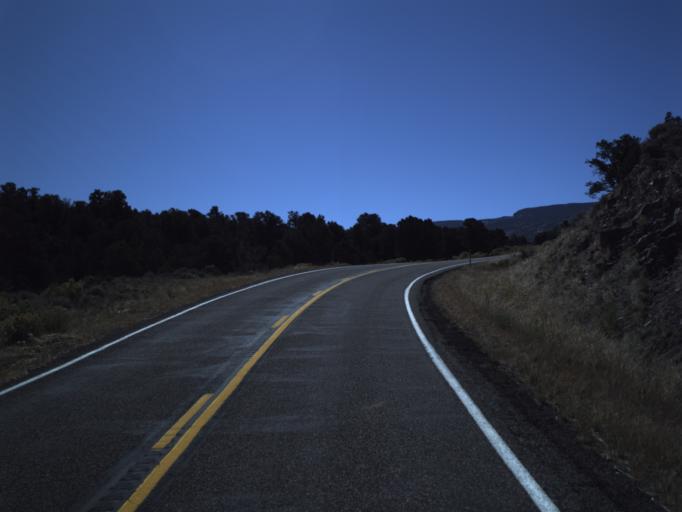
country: US
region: Utah
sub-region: Wayne County
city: Loa
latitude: 38.2457
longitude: -111.3770
